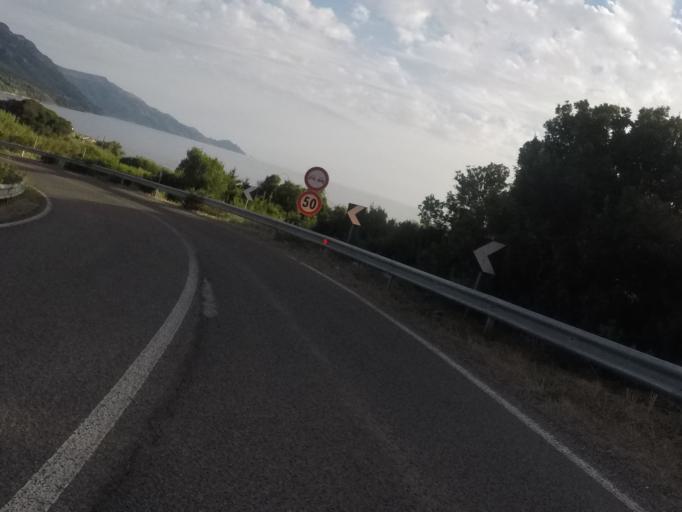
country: IT
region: Sardinia
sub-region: Provincia di Sassari
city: Alghero
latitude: 40.4981
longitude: 8.3679
